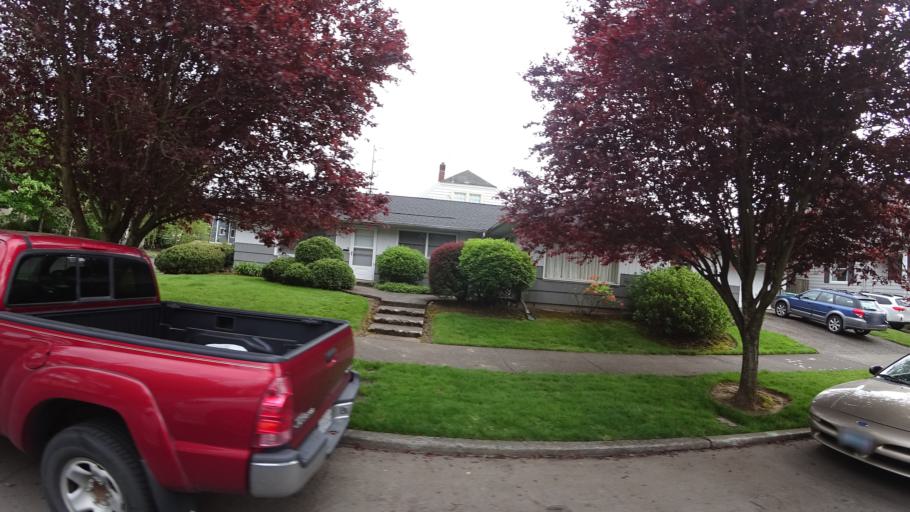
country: US
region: Oregon
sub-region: Clackamas County
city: Milwaukie
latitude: 45.4658
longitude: -122.6553
